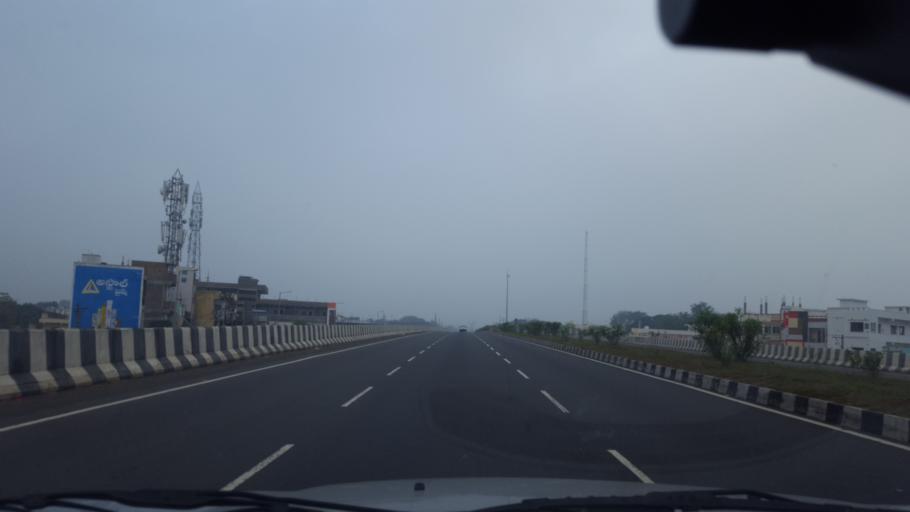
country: IN
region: Andhra Pradesh
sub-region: Prakasam
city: Ongole
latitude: 15.6195
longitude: 80.0219
